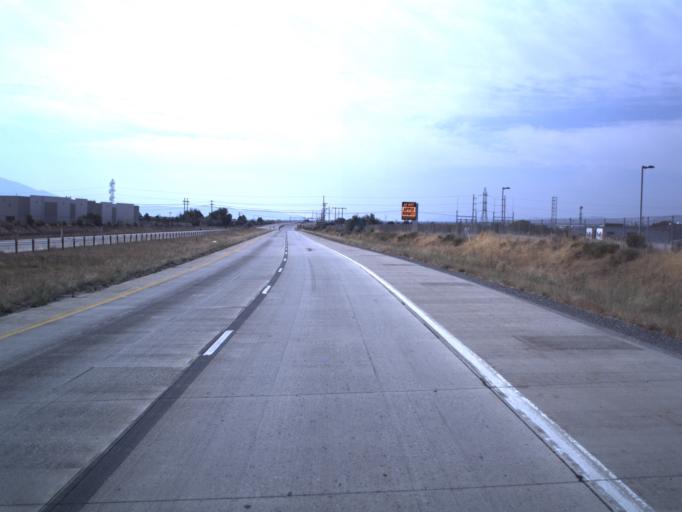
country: US
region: Utah
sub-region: Salt Lake County
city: West Valley City
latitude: 40.7378
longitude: -111.9900
